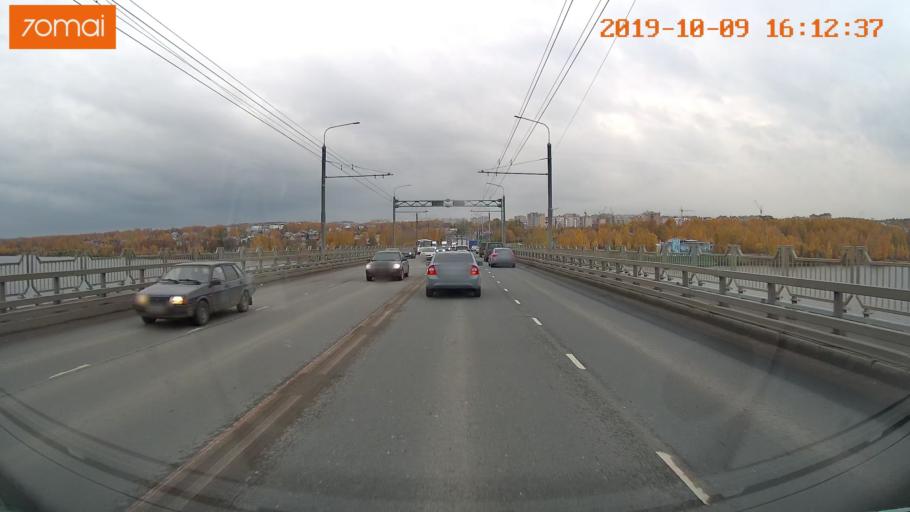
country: RU
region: Kostroma
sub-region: Kostromskoy Rayon
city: Kostroma
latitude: 57.7513
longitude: 40.9367
